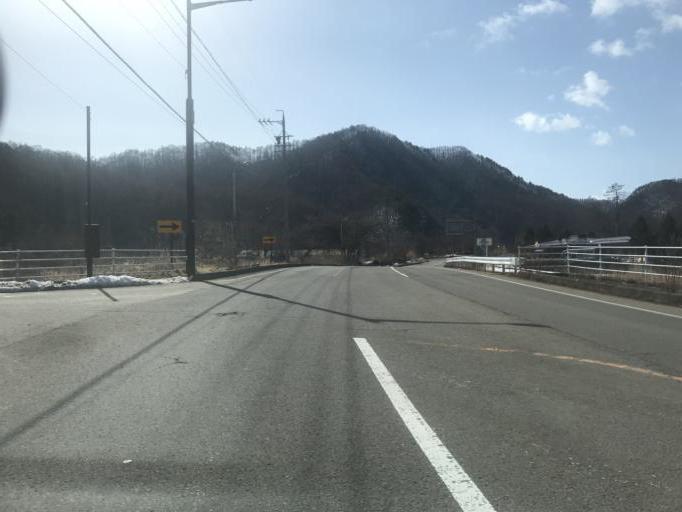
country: JP
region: Nagano
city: Saku
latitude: 36.0198
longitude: 138.4927
